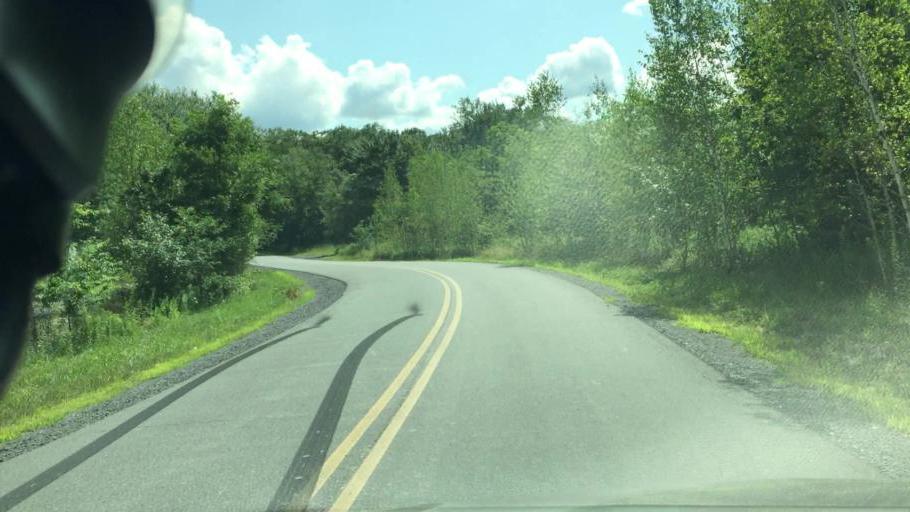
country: US
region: Pennsylvania
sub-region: Luzerne County
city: Freeland
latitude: 41.0292
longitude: -75.9170
